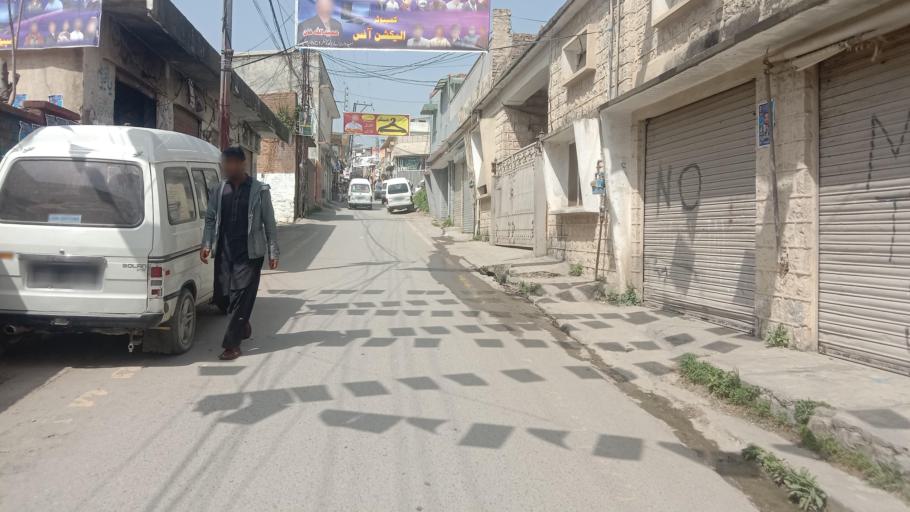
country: PK
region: Khyber Pakhtunkhwa
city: Abbottabad
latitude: 34.1486
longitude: 73.2014
